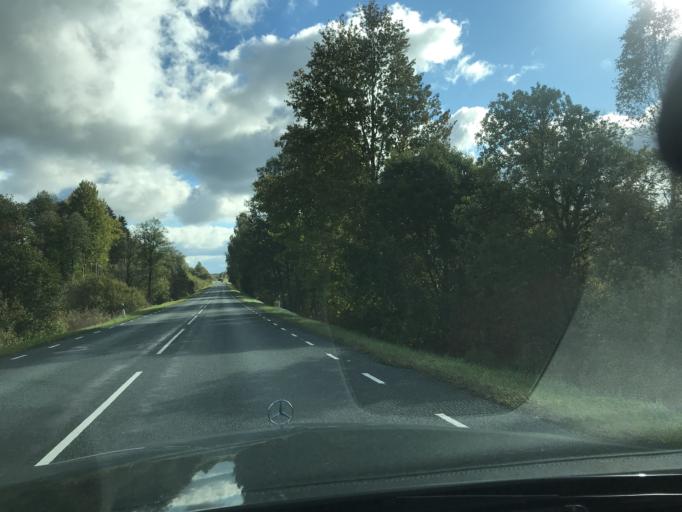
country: EE
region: Vorumaa
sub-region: Antsla vald
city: Vana-Antsla
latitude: 57.9150
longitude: 26.3859
